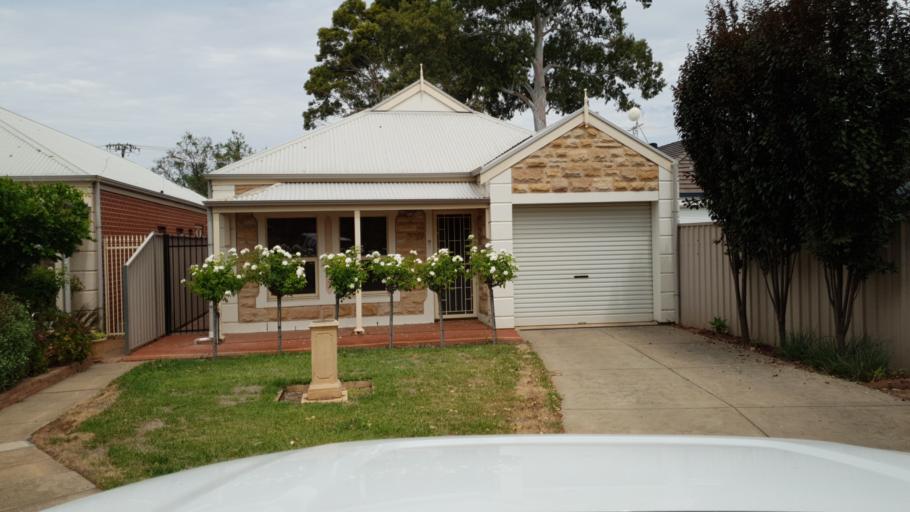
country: AU
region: South Australia
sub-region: Mitcham
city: Clarence Gardens
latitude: -34.9678
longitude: 138.5755
